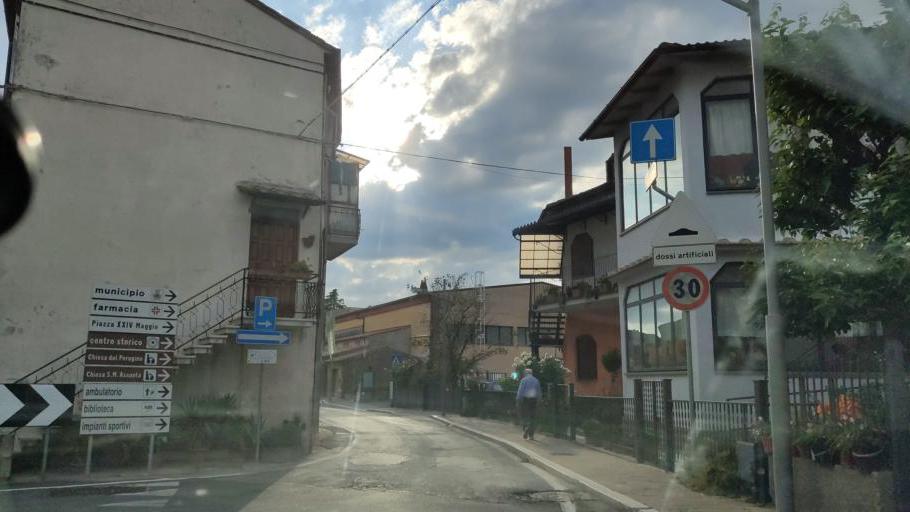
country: IT
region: Umbria
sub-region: Provincia di Terni
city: Giove
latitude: 42.5097
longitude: 12.3285
